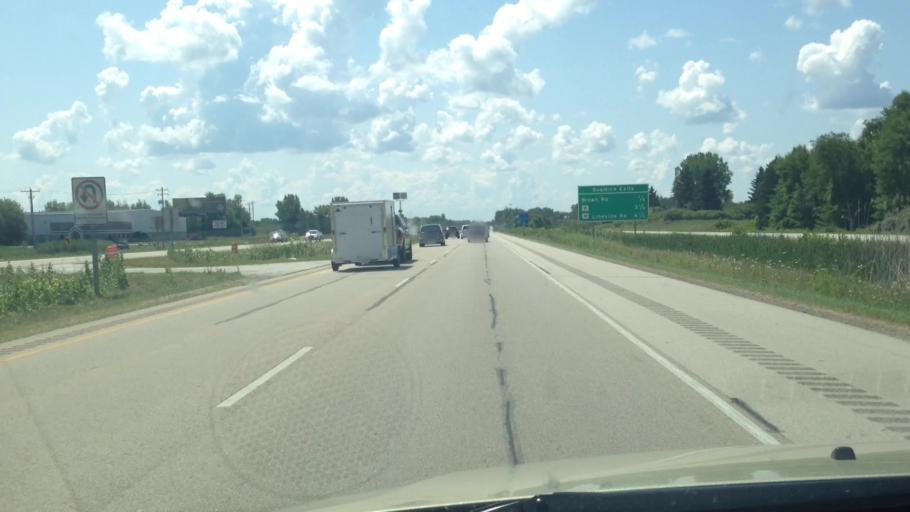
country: US
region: Wisconsin
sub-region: Brown County
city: Suamico
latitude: 44.6877
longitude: -88.0506
